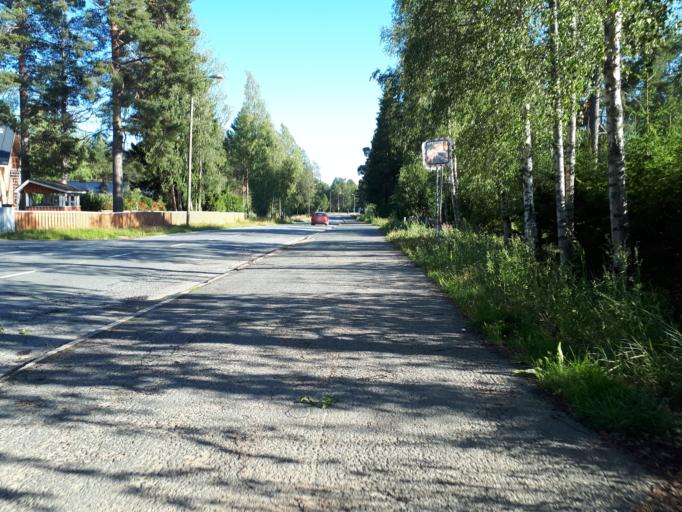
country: FI
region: Northern Ostrobothnia
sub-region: Oulunkaari
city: Ii
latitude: 65.3184
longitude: 25.3846
